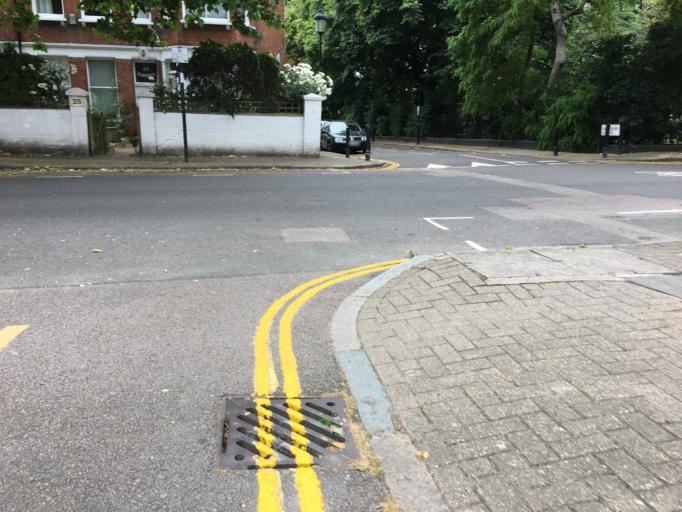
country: GB
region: England
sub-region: Greater London
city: Barnsbury
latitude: 51.5417
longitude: -0.1097
